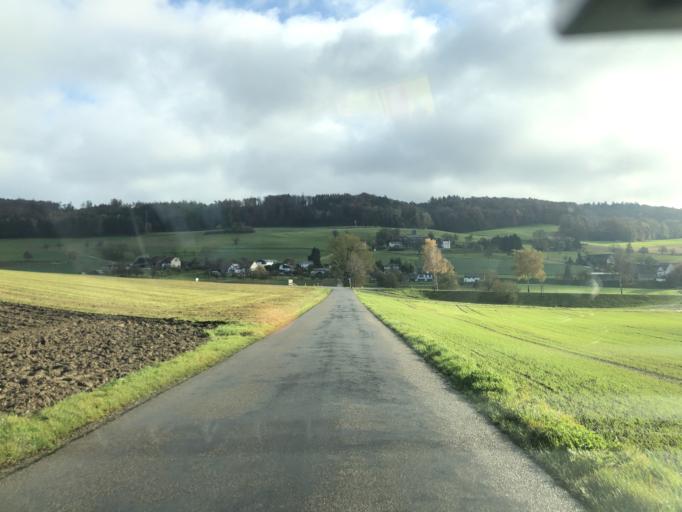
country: CH
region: Aargau
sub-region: Bezirk Baden
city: Unterehrendingen
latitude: 47.5210
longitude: 8.3640
